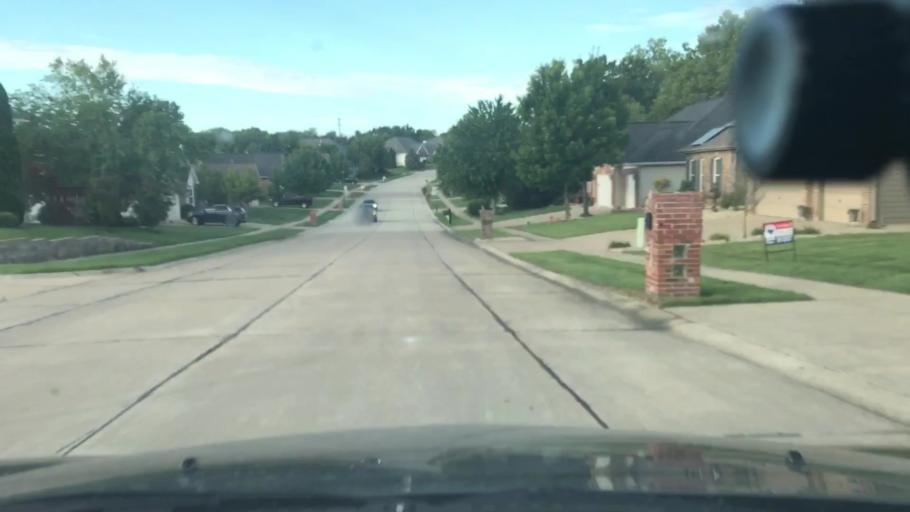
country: US
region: Missouri
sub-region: Saint Charles County
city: Wentzville
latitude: 38.8175
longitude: -90.8999
